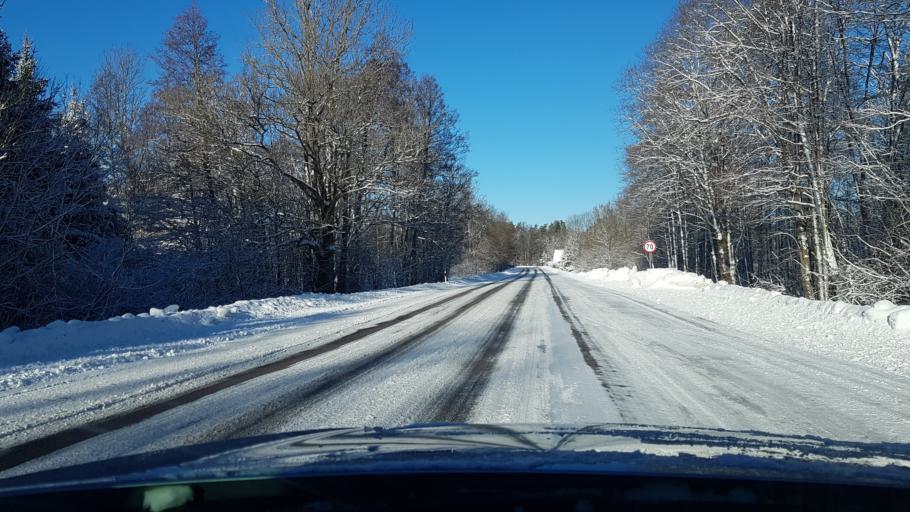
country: EE
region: Hiiumaa
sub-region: Kaerdla linn
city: Kardla
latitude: 58.9193
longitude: 22.7944
